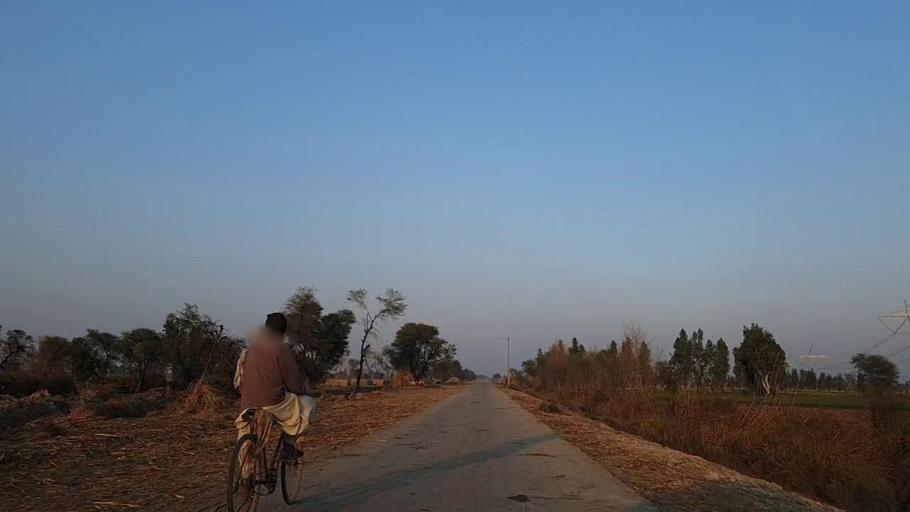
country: PK
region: Sindh
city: Naushahro Firoz
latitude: 26.7718
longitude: 68.0584
